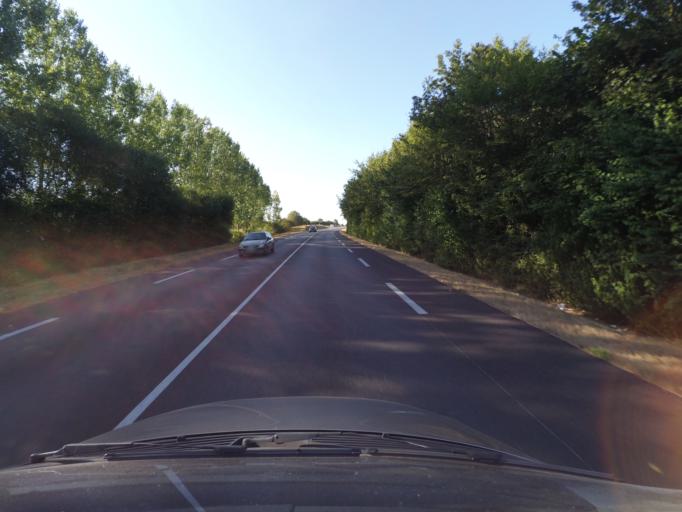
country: FR
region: Pays de la Loire
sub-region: Departement de la Vendee
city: Bouffere
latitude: 46.9675
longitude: -1.3505
